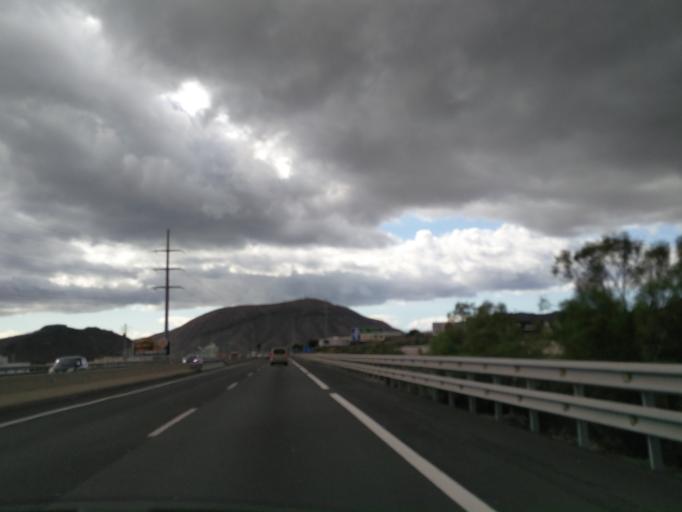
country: ES
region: Canary Islands
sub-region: Provincia de Santa Cruz de Tenerife
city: Las Rosas
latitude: 28.0531
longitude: -16.6510
